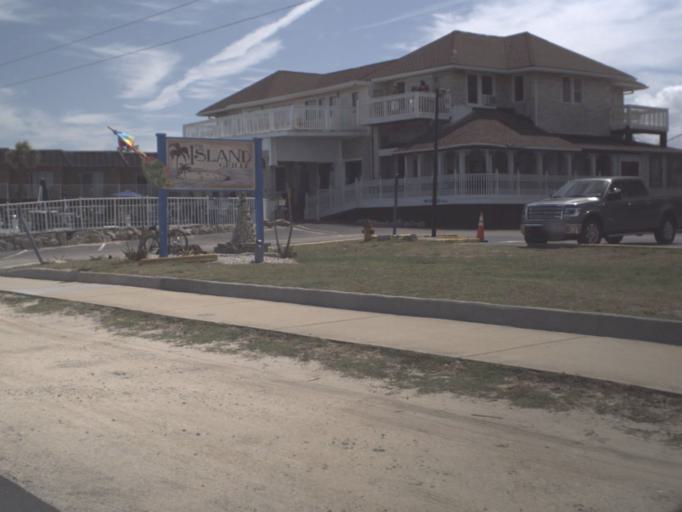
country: US
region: Florida
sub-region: Flagler County
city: Flagler Beach
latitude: 29.4735
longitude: -81.1238
